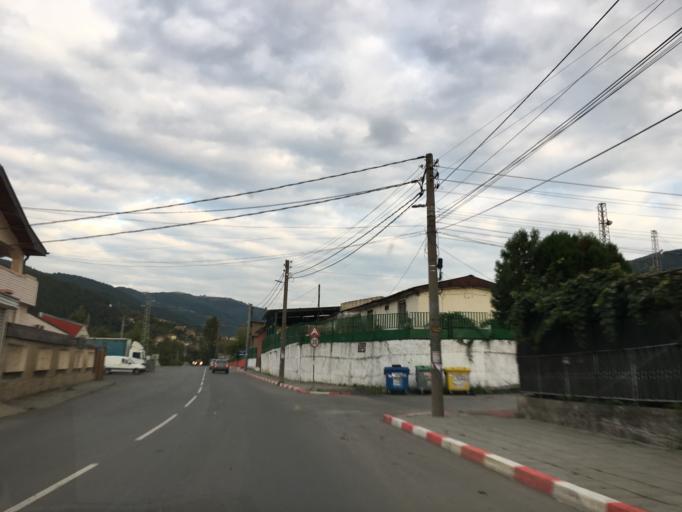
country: BG
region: Sofiya
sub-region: Obshtina Svoge
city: Svoge
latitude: 42.9612
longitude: 23.3481
